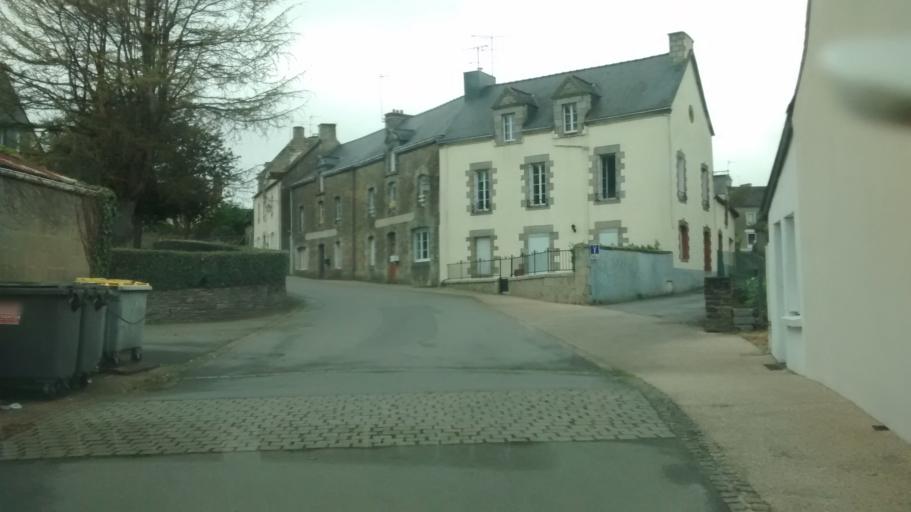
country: FR
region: Brittany
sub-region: Departement du Morbihan
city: Serent
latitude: 47.8227
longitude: -2.5037
